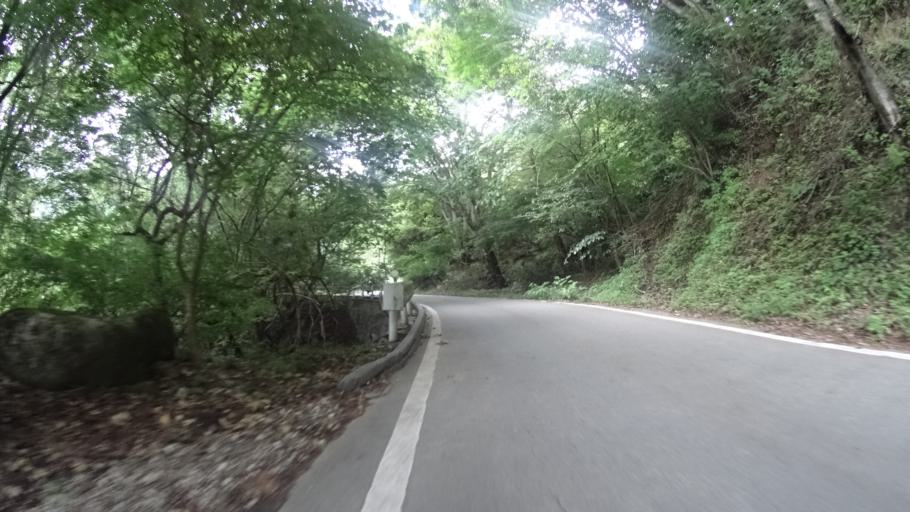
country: JP
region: Yamanashi
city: Enzan
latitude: 35.7901
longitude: 138.6876
